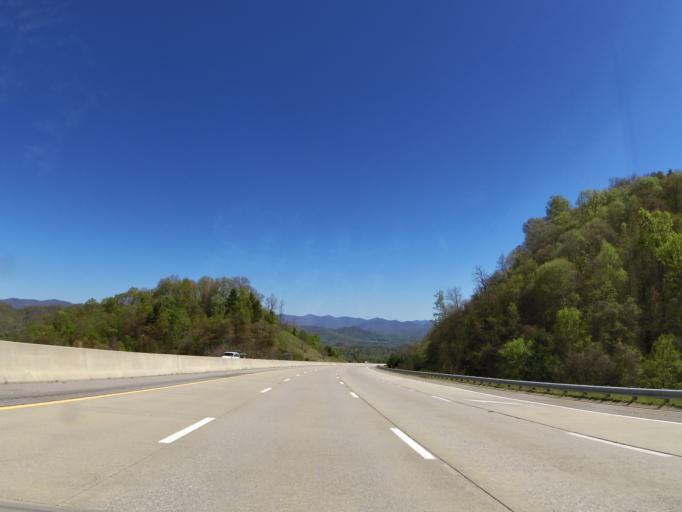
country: US
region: North Carolina
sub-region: Madison County
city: Mars Hill
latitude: 35.8716
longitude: -82.5392
